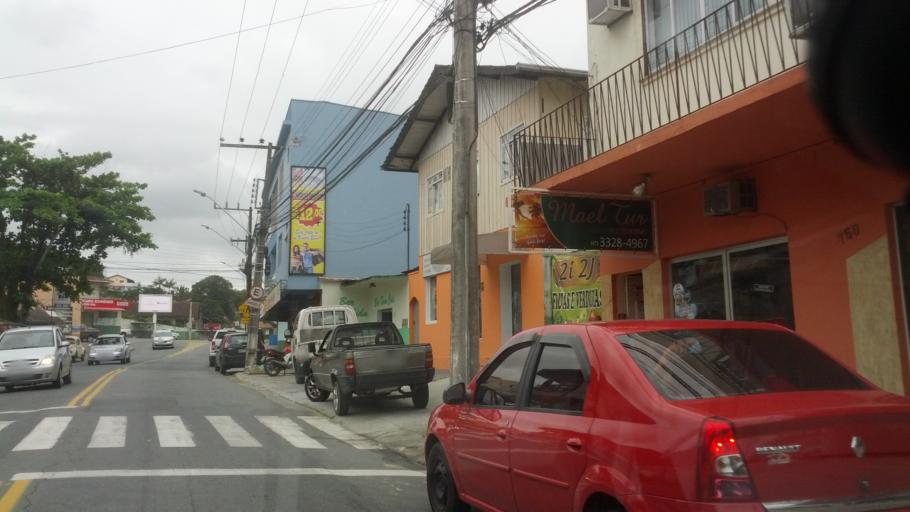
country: BR
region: Santa Catarina
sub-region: Blumenau
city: Blumenau
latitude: -26.9122
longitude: -49.0998
